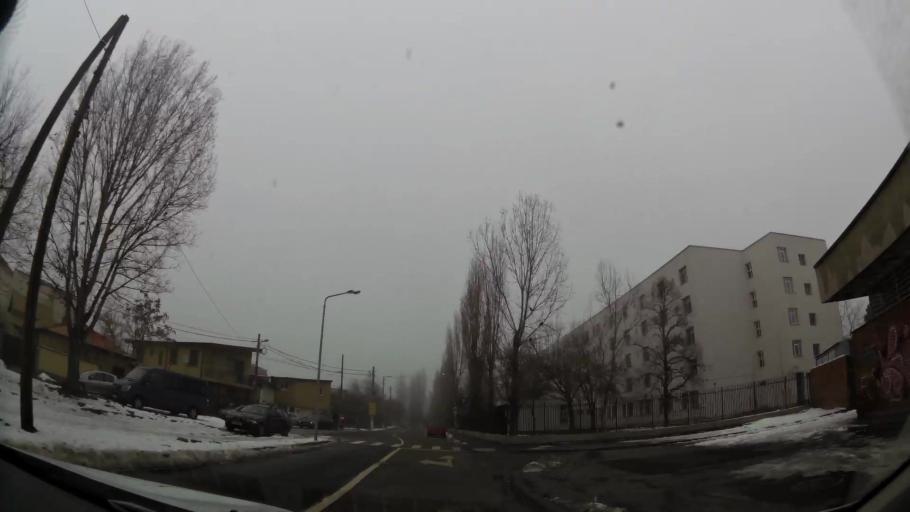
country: RO
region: Ilfov
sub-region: Comuna Chiajna
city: Rosu
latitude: 44.4642
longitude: 26.0413
